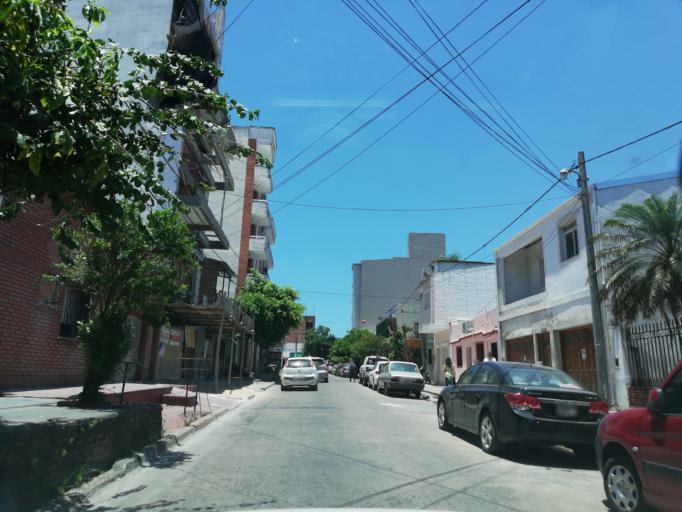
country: AR
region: Corrientes
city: Corrientes
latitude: -27.4651
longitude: -58.8273
